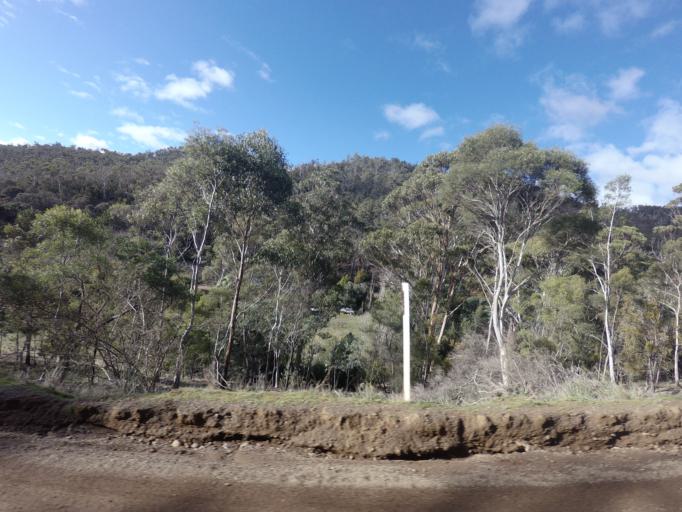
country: AU
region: Tasmania
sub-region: Derwent Valley
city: New Norfolk
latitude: -42.8179
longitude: 147.1278
